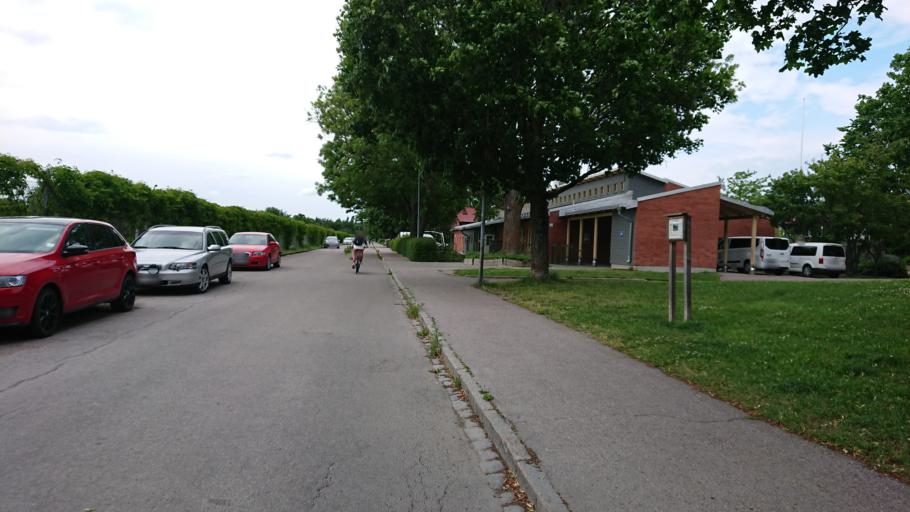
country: SE
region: Uppsala
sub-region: Uppsala Kommun
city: Uppsala
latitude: 59.8747
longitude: 17.6157
